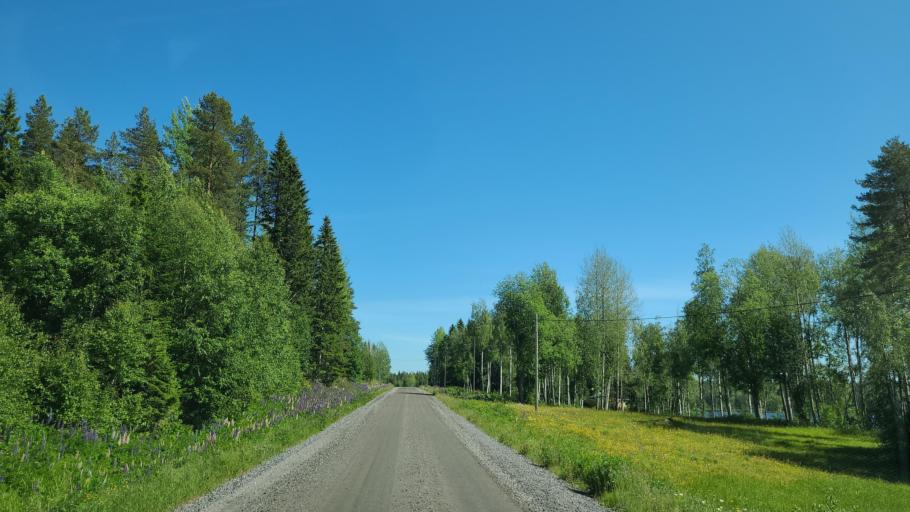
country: SE
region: Vaesterbotten
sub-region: Bjurholms Kommun
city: Bjurholm
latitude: 63.6406
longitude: 19.1386
